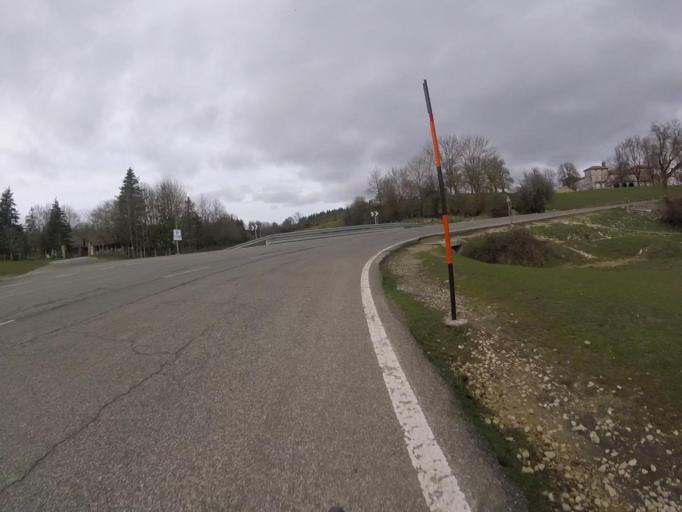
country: ES
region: Navarre
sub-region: Provincia de Navarra
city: Eulate
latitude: 42.8169
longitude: -2.1661
